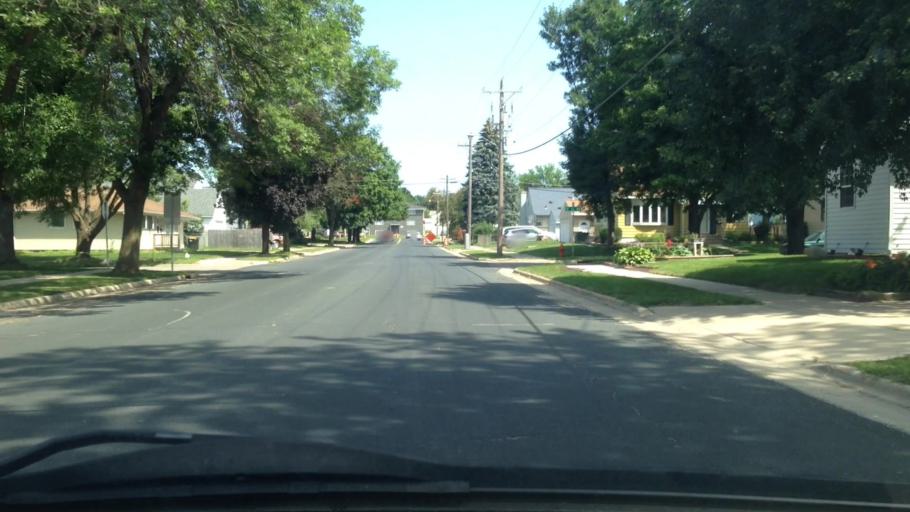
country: US
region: Minnesota
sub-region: Olmsted County
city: Rochester
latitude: 44.0414
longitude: -92.4926
